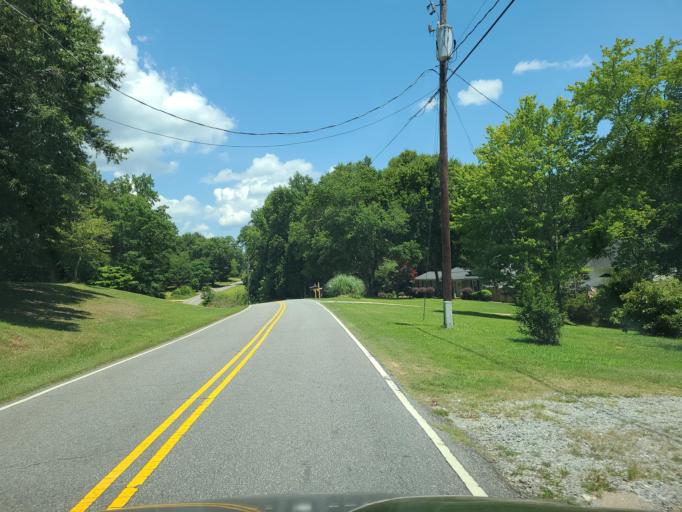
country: US
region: South Carolina
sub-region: Spartanburg County
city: Inman Mills
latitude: 35.0338
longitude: -82.1765
